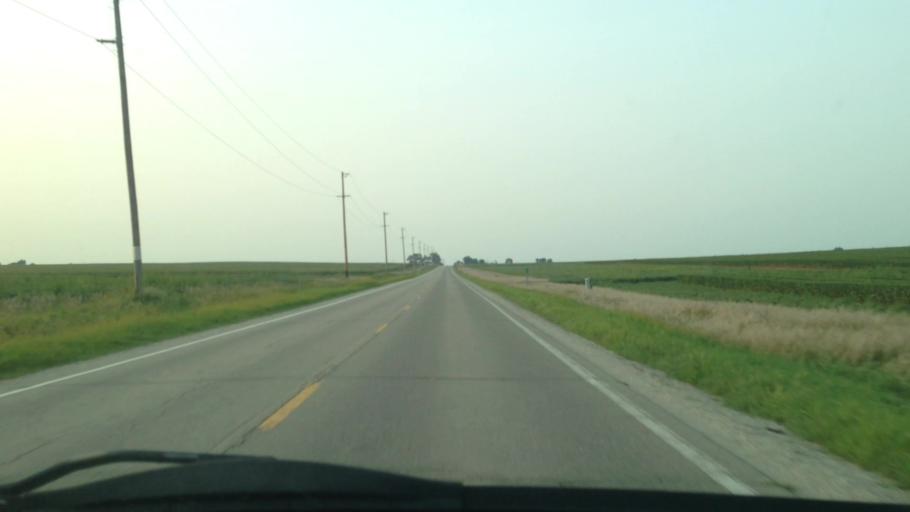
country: US
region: Iowa
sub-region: Iowa County
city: Marengo
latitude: 41.9514
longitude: -92.0852
